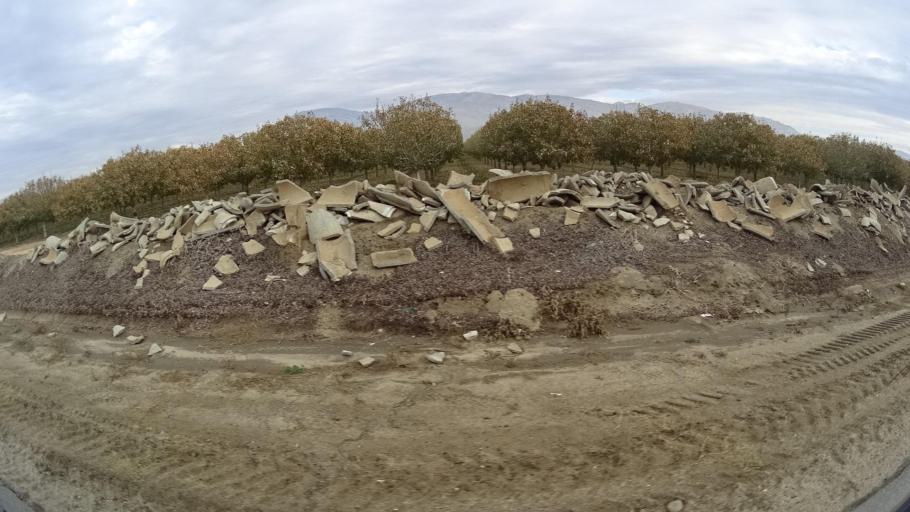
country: US
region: California
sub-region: Kern County
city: Arvin
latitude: 35.1637
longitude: -118.8237
